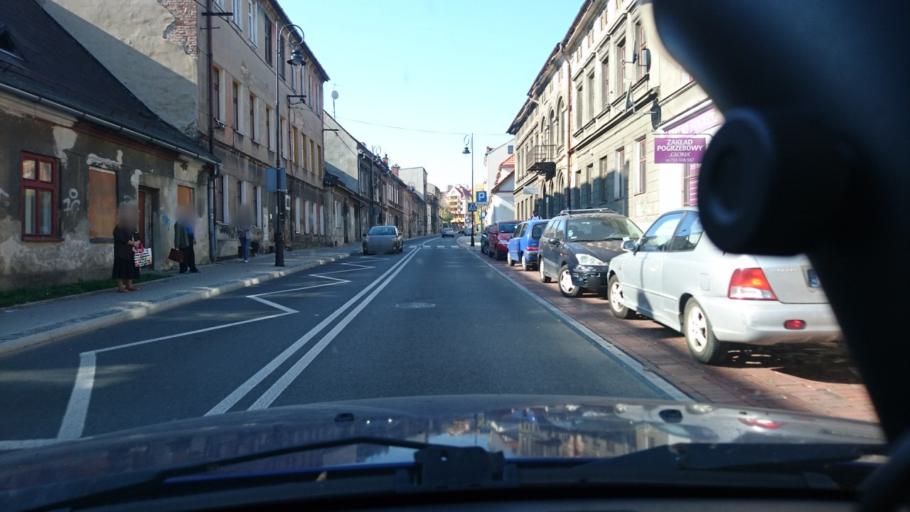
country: PL
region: Silesian Voivodeship
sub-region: Bielsko-Biala
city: Bielsko-Biala
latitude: 49.8206
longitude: 19.0386
